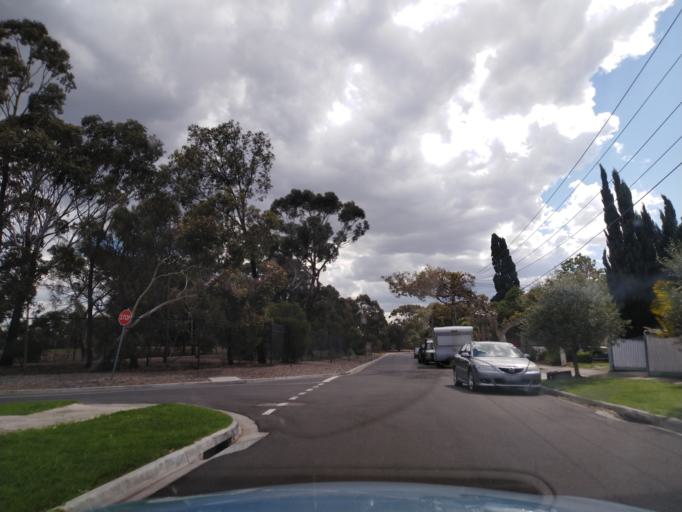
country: AU
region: Victoria
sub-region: Hobsons Bay
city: South Kingsville
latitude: -37.8346
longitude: 144.8713
